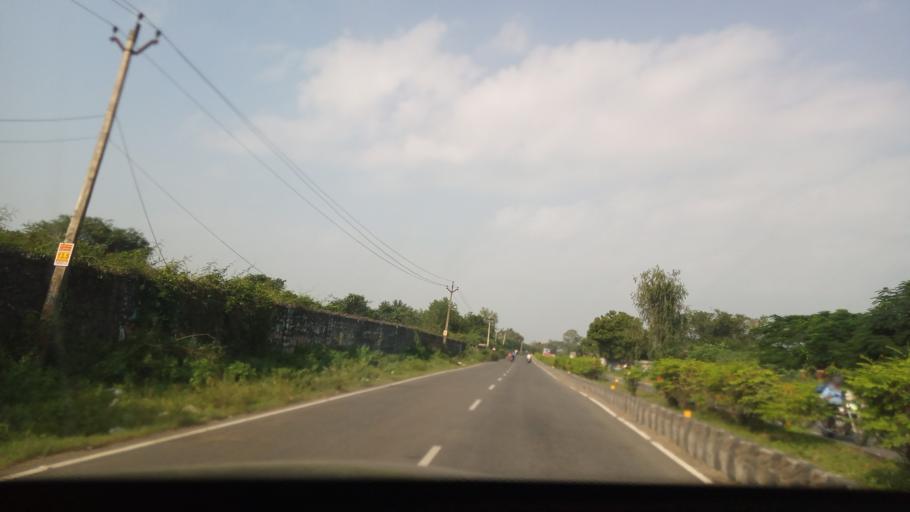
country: IN
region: Tamil Nadu
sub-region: Kancheepuram
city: Vandalur
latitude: 12.8719
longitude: 80.0986
